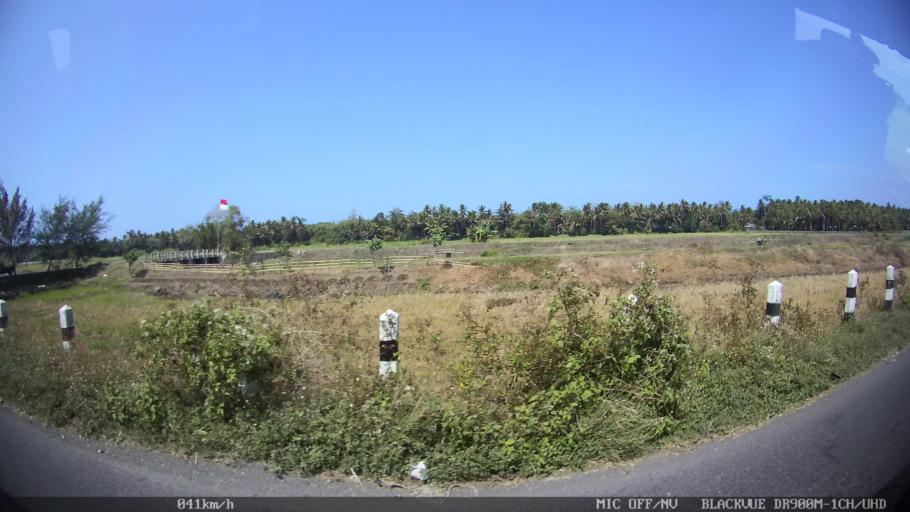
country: ID
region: Daerah Istimewa Yogyakarta
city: Srandakan
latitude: -7.9516
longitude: 110.1899
